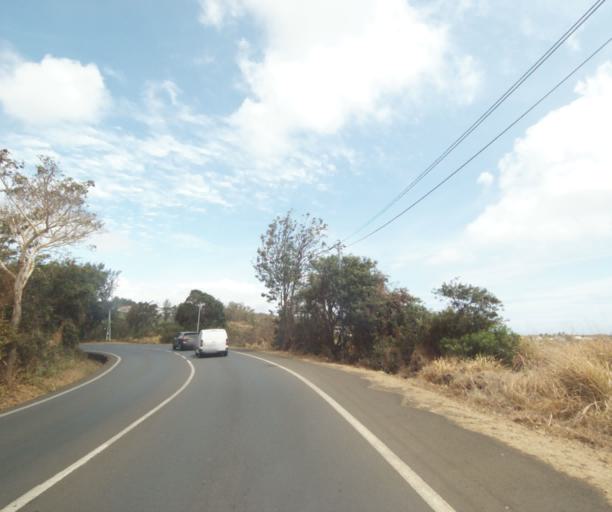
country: RE
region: Reunion
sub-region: Reunion
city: Trois-Bassins
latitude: -21.0685
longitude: 55.2665
